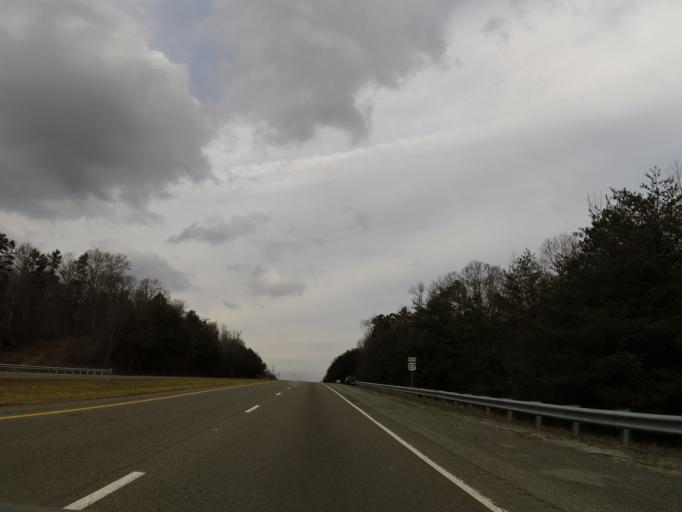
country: US
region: Tennessee
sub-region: Hamilton County
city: Sale Creek
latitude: 35.3121
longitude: -85.1407
